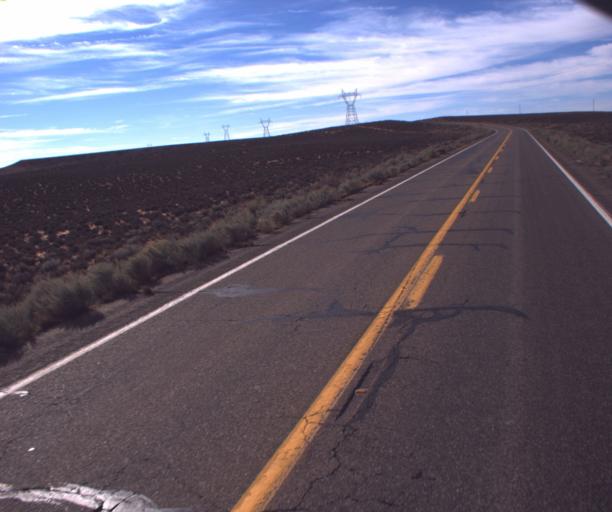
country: US
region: Arizona
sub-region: Coconino County
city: LeChee
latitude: 36.8109
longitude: -111.3062
